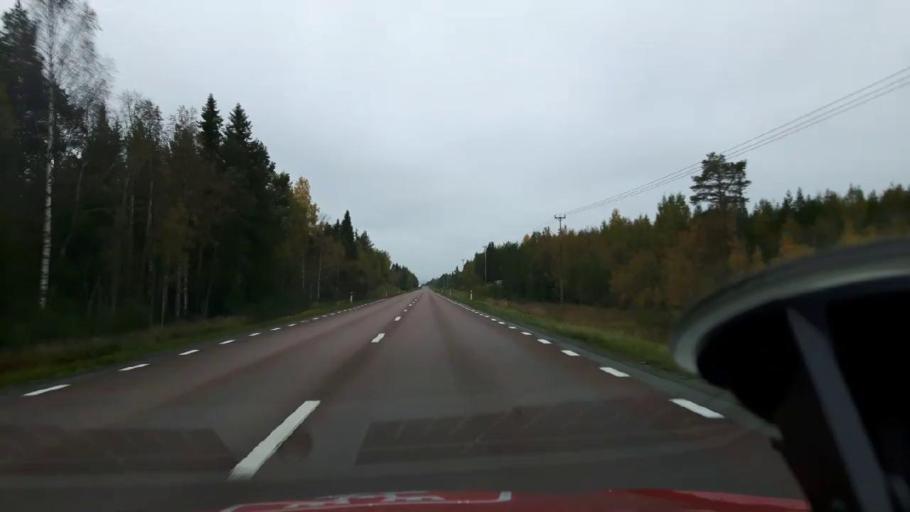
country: SE
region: Jaemtland
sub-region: Bergs Kommun
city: Hoverberg
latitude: 62.8624
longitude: 14.5185
